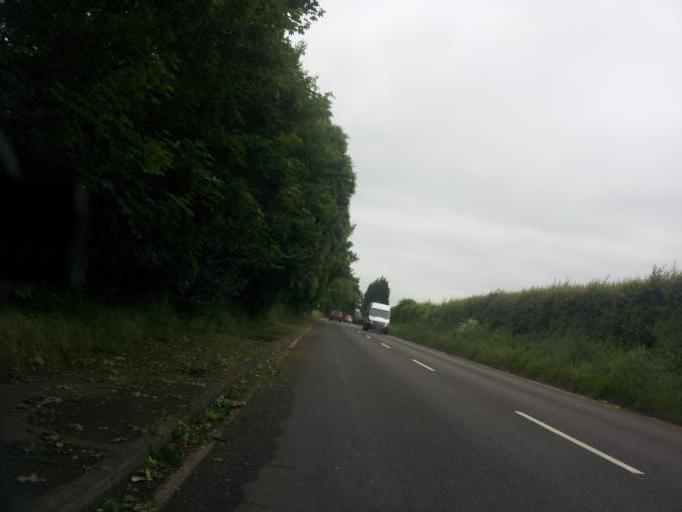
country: GB
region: England
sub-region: Kent
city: Wateringbury
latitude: 51.2545
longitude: 0.4654
